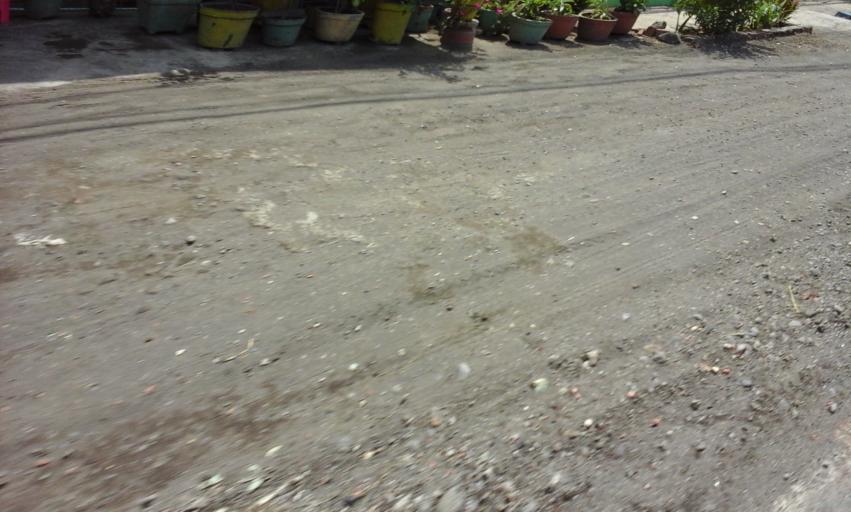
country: ID
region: East Java
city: Klatakan
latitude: -8.1400
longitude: 114.3988
